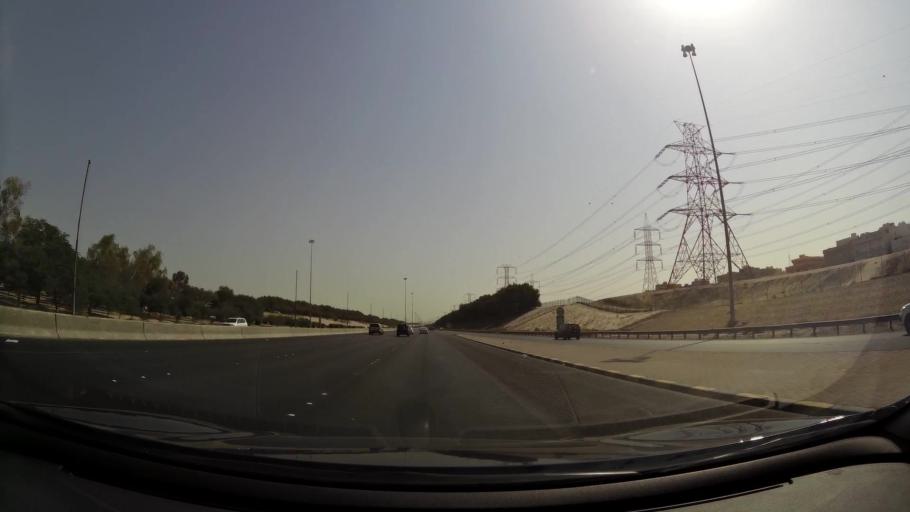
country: KW
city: Bayan
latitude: 29.3036
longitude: 48.0235
